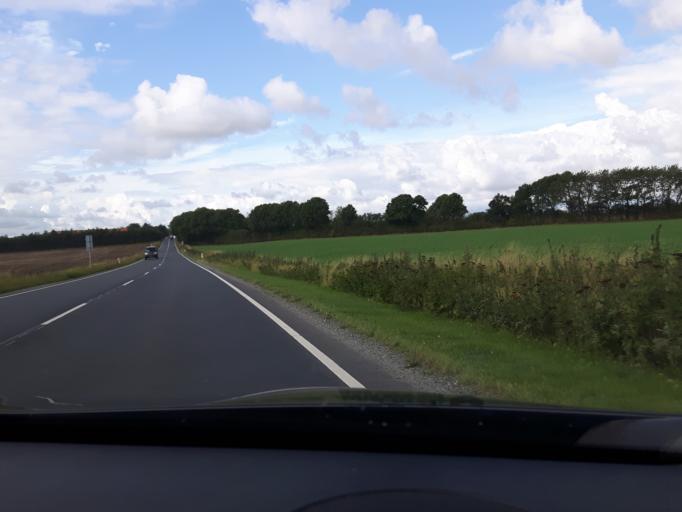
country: DK
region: Central Jutland
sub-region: Hedensted Kommune
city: Hedensted
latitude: 55.7341
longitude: 9.6782
